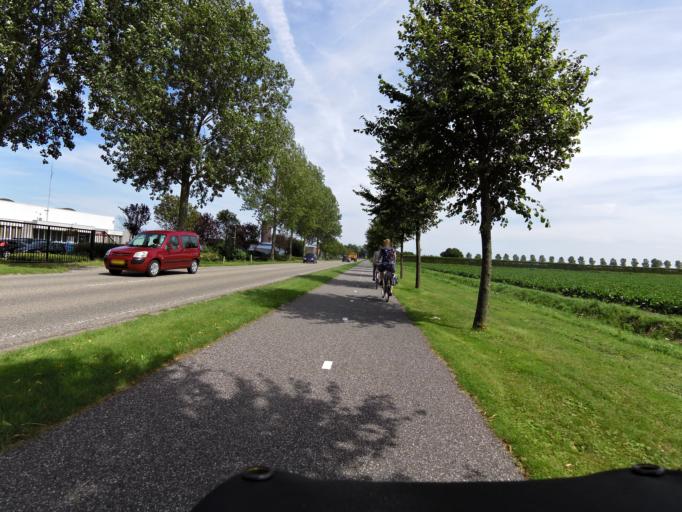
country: NL
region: South Holland
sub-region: Gemeente Goeree-Overflakkee
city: Dirksland
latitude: 51.7487
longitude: 4.1149
